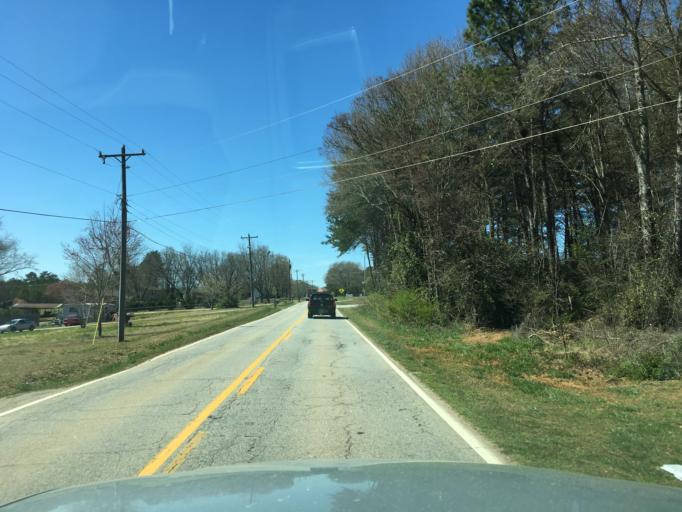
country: US
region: South Carolina
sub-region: Spartanburg County
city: Roebuck
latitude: 34.8881
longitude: -81.9756
